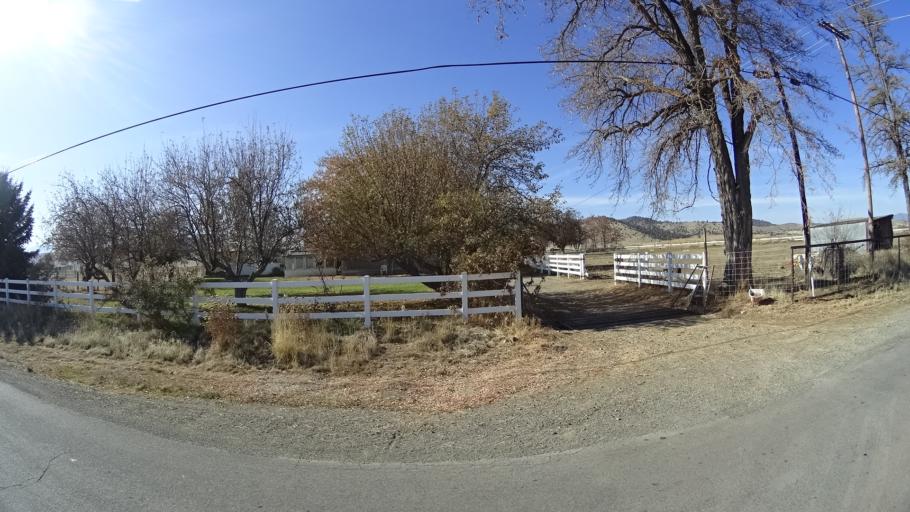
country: US
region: California
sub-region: Siskiyou County
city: Montague
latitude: 41.6206
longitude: -122.5225
